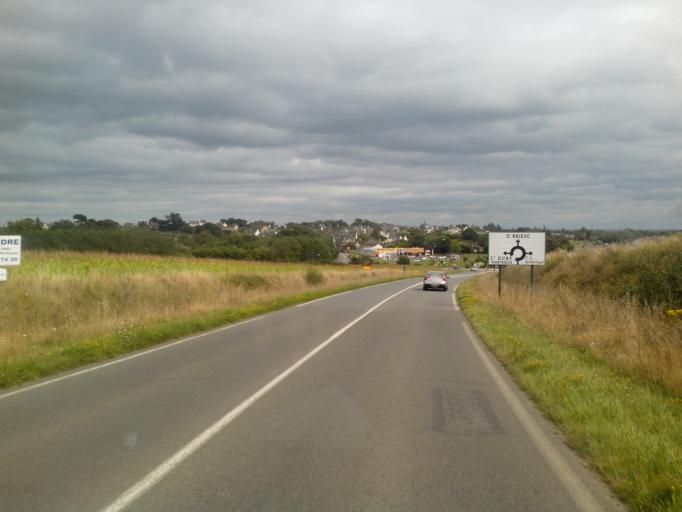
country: FR
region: Brittany
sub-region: Departement des Cotes-d'Armor
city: Saint-Quay-Portrieux
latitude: 48.6594
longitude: -2.8634
